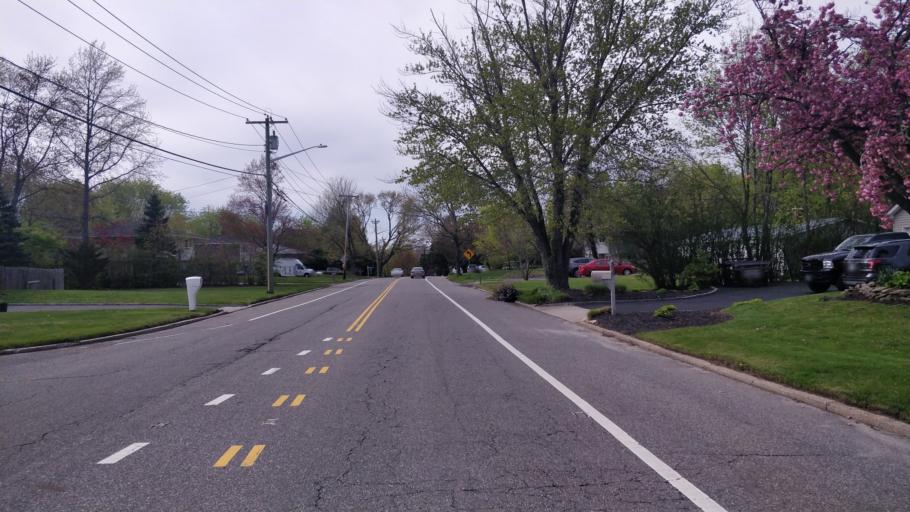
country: US
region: New York
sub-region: Suffolk County
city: Setauket-East Setauket
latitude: 40.9245
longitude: -73.0823
